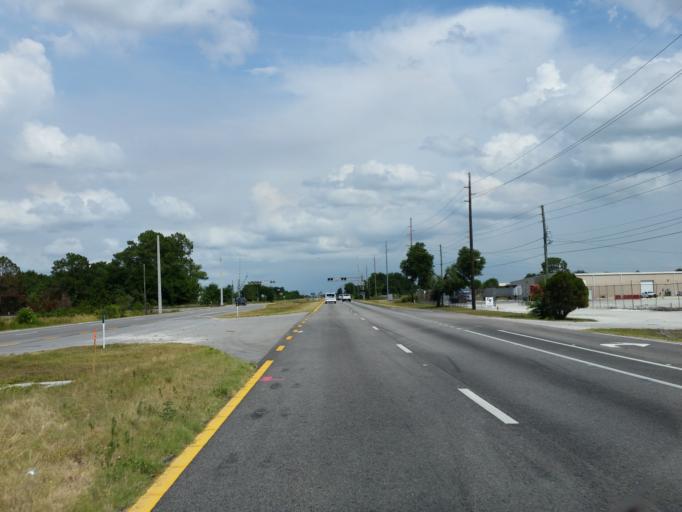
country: US
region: Florida
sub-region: Polk County
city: Alturas
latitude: 27.9036
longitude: -81.6610
